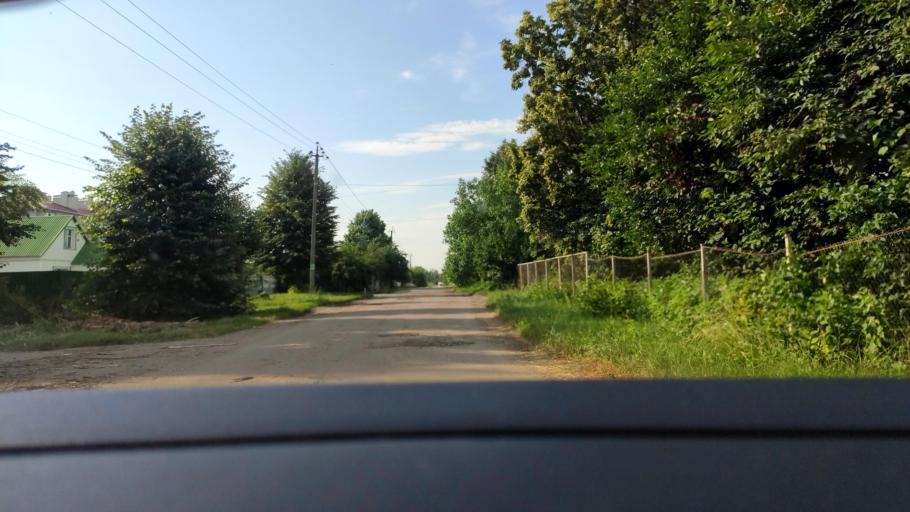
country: RU
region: Voronezj
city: Maslovka
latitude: 51.5369
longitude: 39.3359
